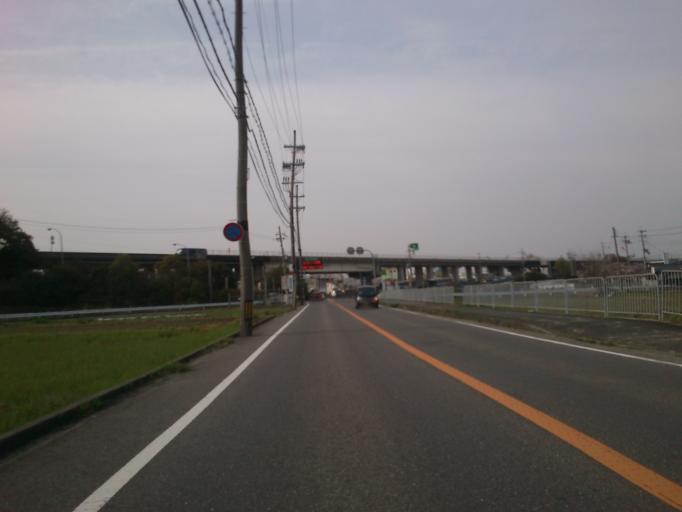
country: JP
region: Kyoto
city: Tanabe
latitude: 34.8354
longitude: 135.7539
